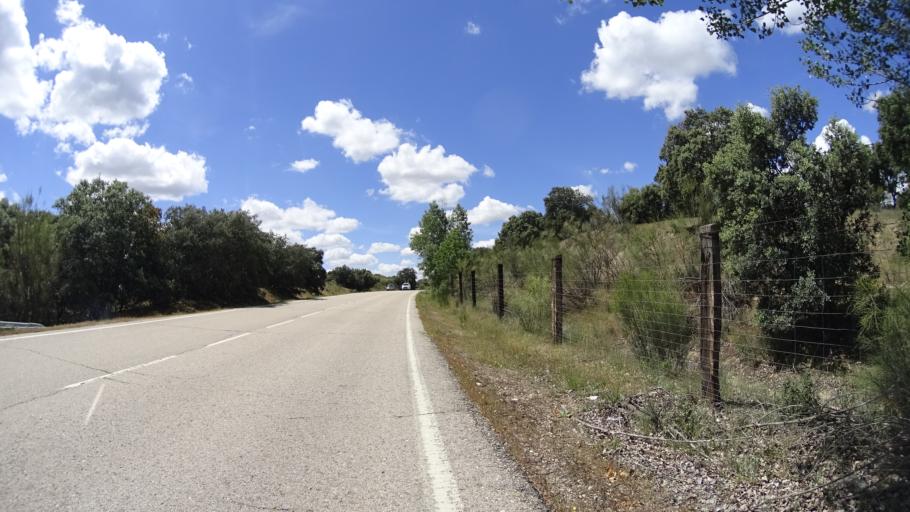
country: ES
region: Madrid
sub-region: Provincia de Madrid
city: Villanueva del Pardillo
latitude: 40.4563
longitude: -3.9487
